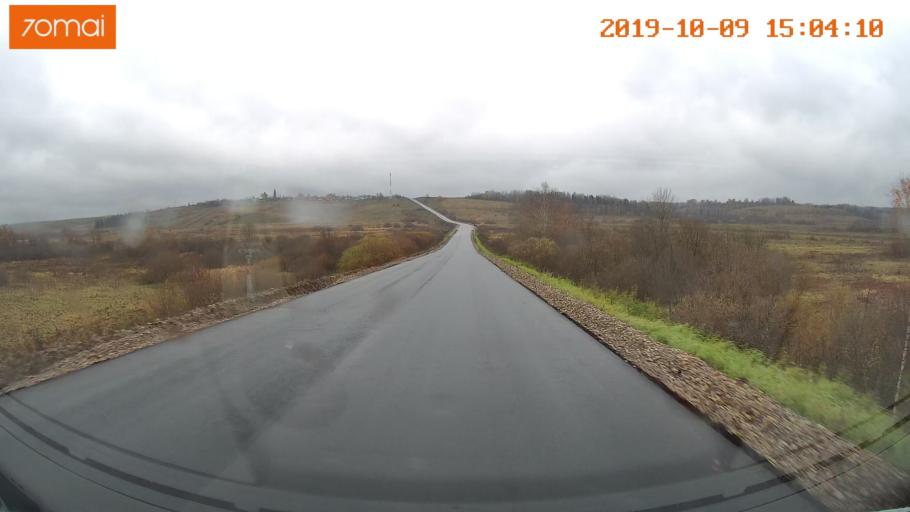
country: RU
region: Kostroma
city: Chistyye Bory
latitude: 58.2619
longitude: 41.6696
